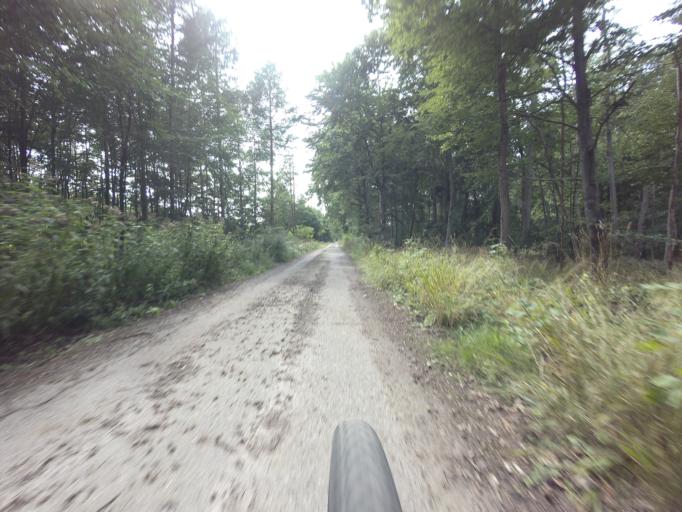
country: DK
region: Zealand
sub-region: Faxe Kommune
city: Fakse Ladeplads
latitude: 55.2345
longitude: 12.1926
